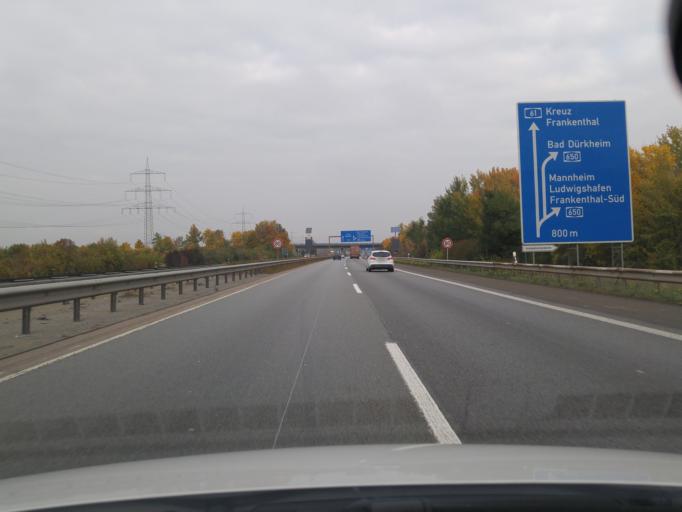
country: DE
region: Rheinland-Pfalz
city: Fussgonheim
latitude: 49.4645
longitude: 8.3136
